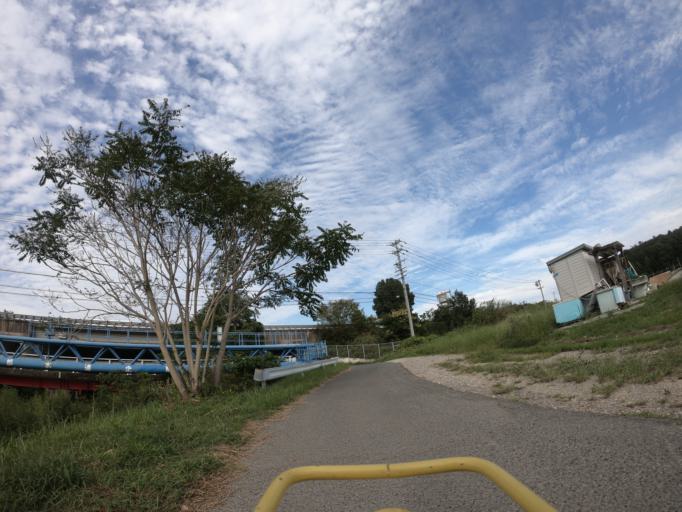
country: JP
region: Aichi
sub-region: Toyota-shi
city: Toyota
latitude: 35.1344
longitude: 137.0737
